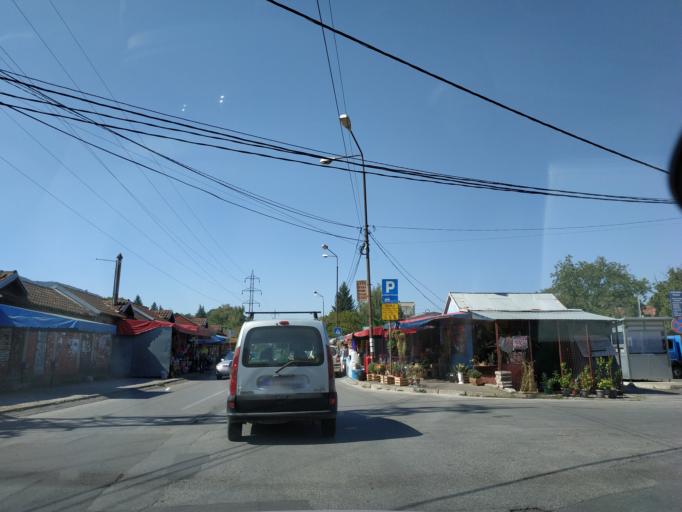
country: RS
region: Central Serbia
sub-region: Sumadijski Okrug
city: Arangelovac
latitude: 44.3011
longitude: 20.5716
